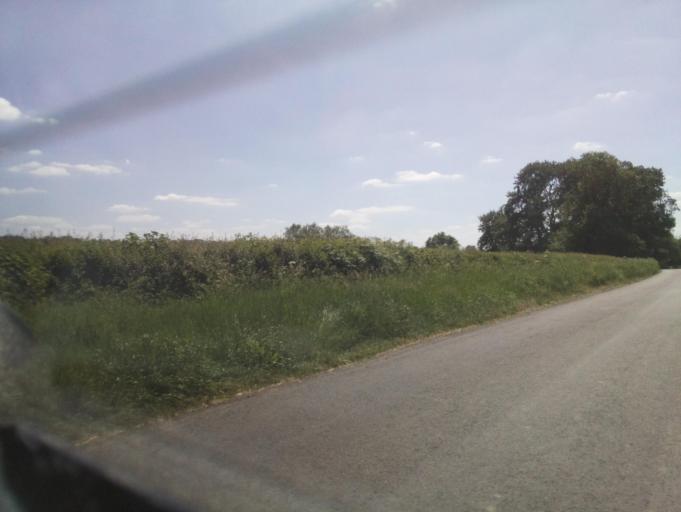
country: GB
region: England
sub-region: Wiltshire
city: Royal Wootton Bassett
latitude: 51.4989
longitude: -1.9150
